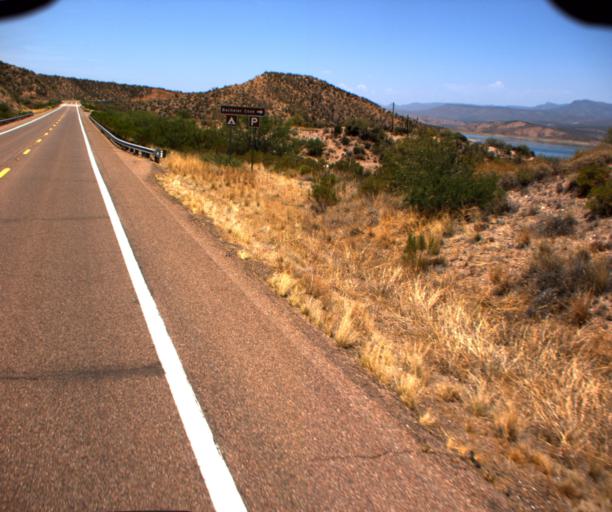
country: US
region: Arizona
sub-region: Gila County
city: Tonto Basin
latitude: 33.7113
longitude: -111.2001
